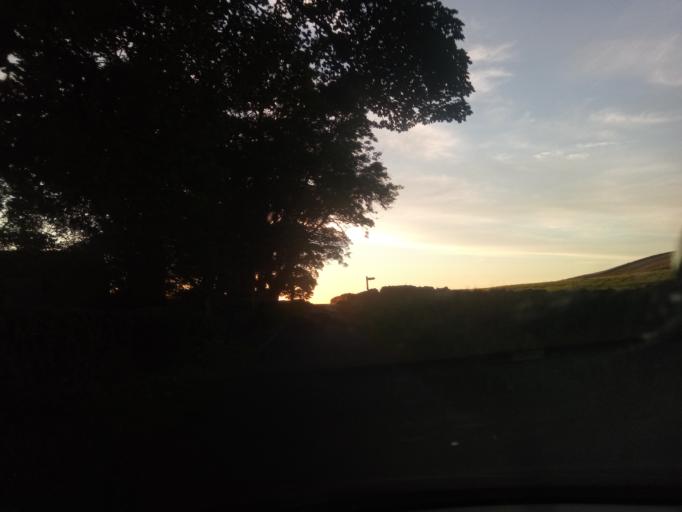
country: GB
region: England
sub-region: Northumberland
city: Bardon Mill
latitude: 54.7997
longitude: -2.3547
